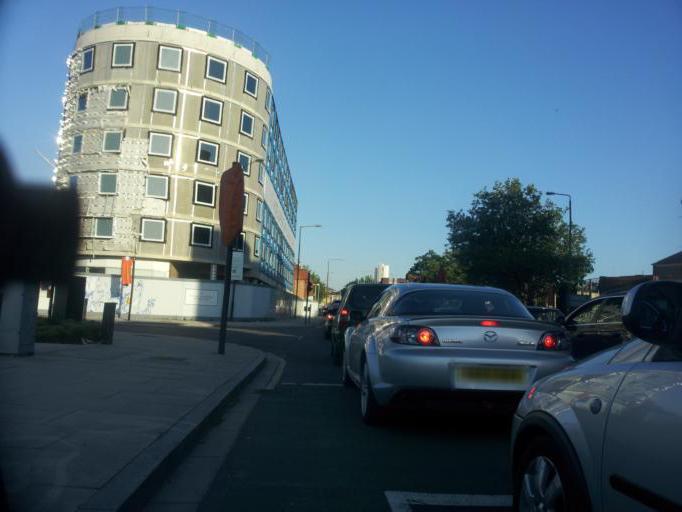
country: GB
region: England
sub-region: Greater London
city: Woolwich
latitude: 51.4931
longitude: 0.0667
